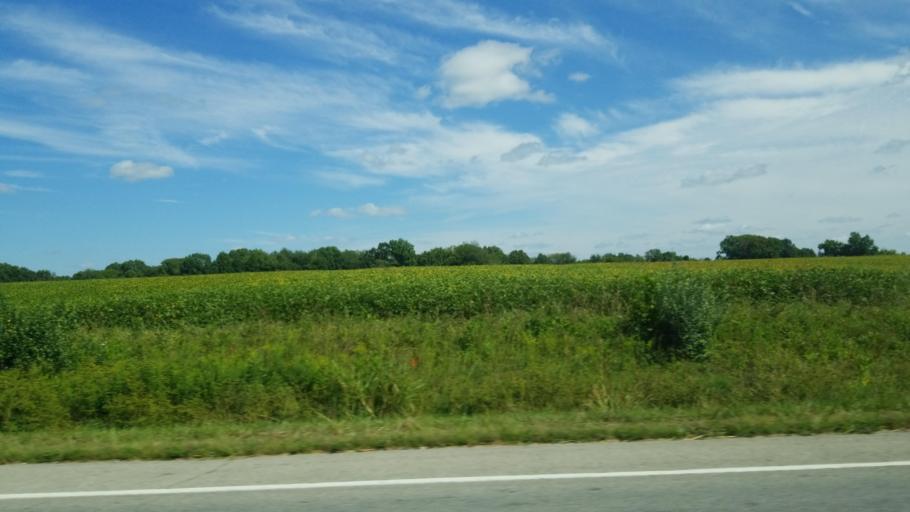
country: US
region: Illinois
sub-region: Williamson County
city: Marion
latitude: 37.7687
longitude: -88.9328
